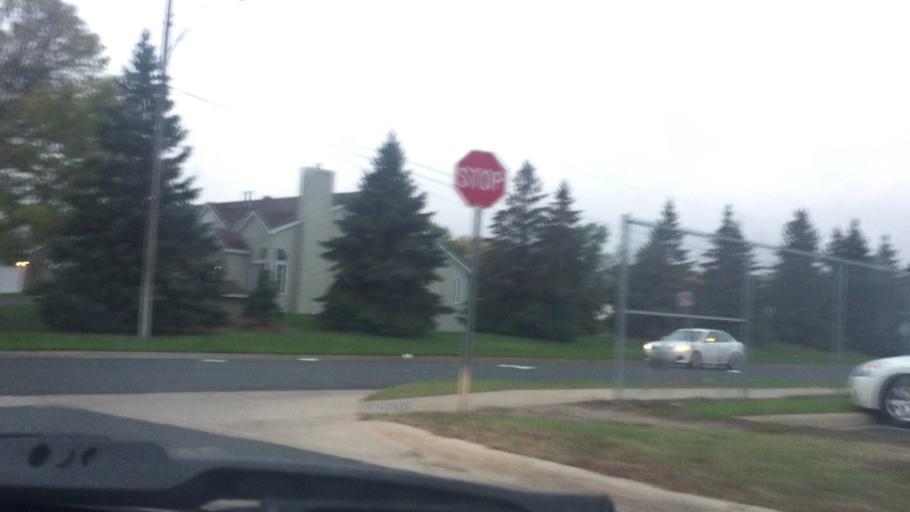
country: US
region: Minnesota
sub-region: Anoka County
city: Spring Lake Park
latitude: 45.1116
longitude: -93.2448
